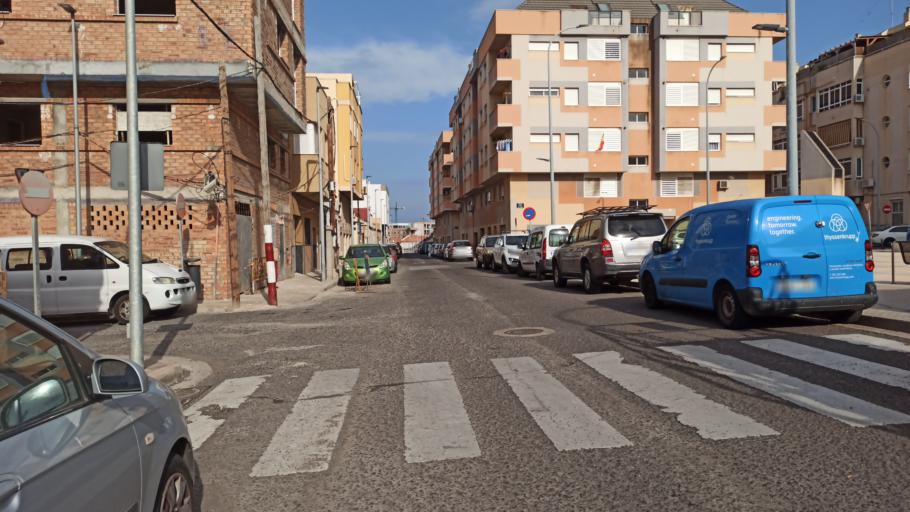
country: ES
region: Melilla
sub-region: Melilla
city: Melilla
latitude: 35.2829
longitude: -2.9490
